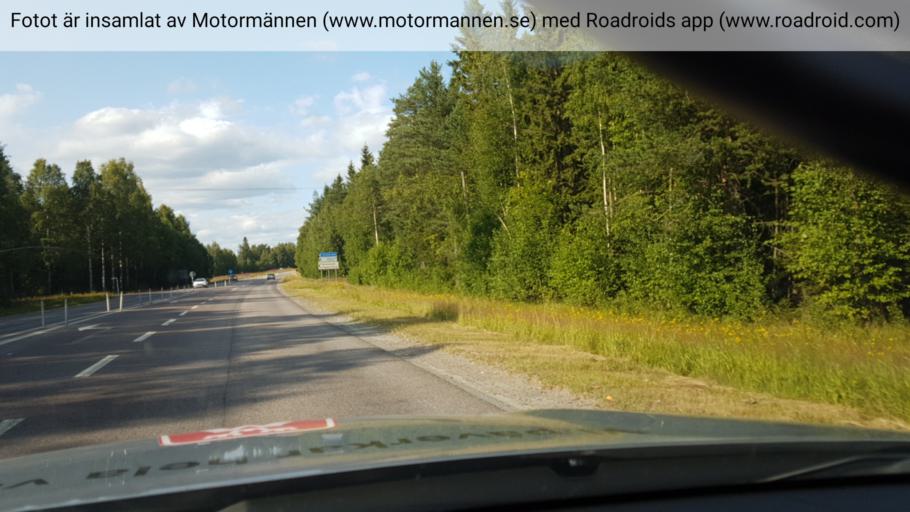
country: SE
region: Norrbotten
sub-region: Pitea Kommun
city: Pitea
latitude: 65.2811
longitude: 21.5103
